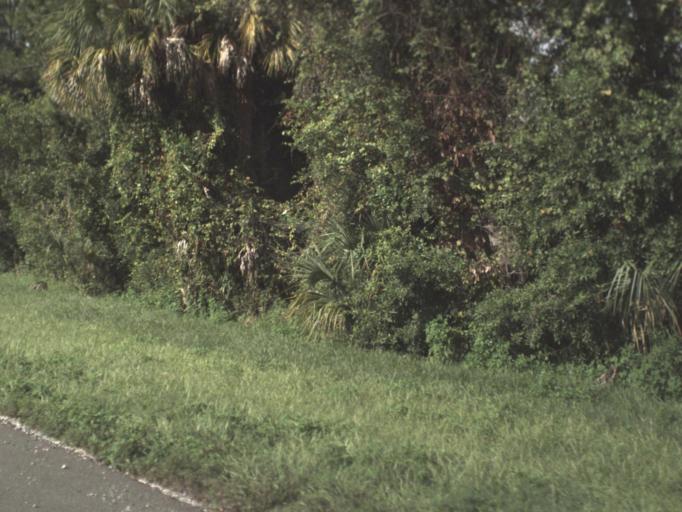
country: US
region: Florida
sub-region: Pasco County
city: Shady Hills
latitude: 28.3402
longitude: -82.5016
